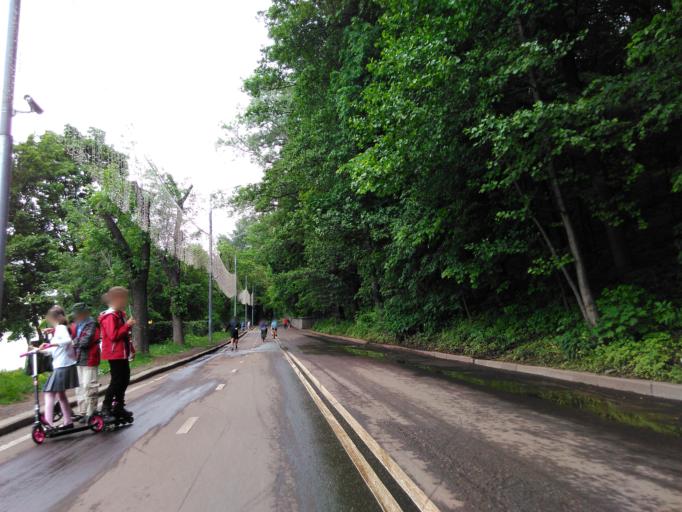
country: RU
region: Moscow
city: Novyye Cheremushki
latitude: 55.7175
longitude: 37.5850
